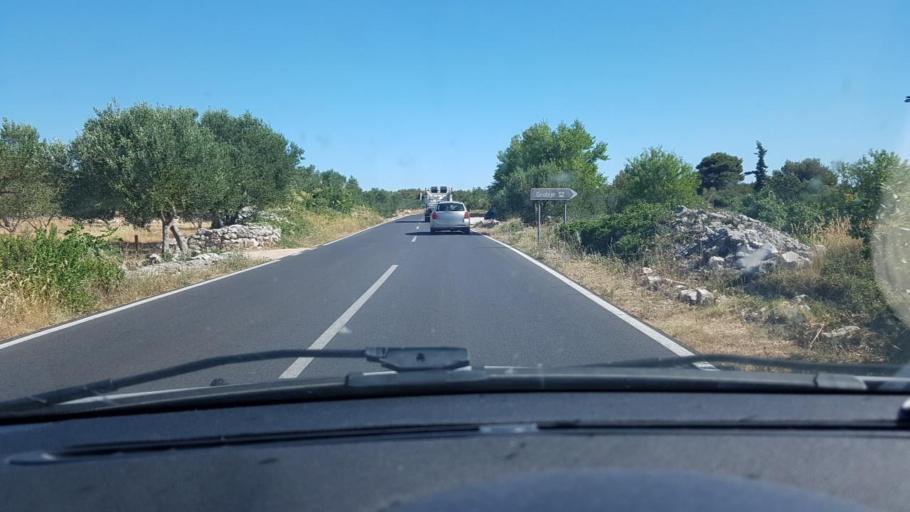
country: HR
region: Sibensko-Kniniska
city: Vodice
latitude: 43.7526
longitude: 15.8147
